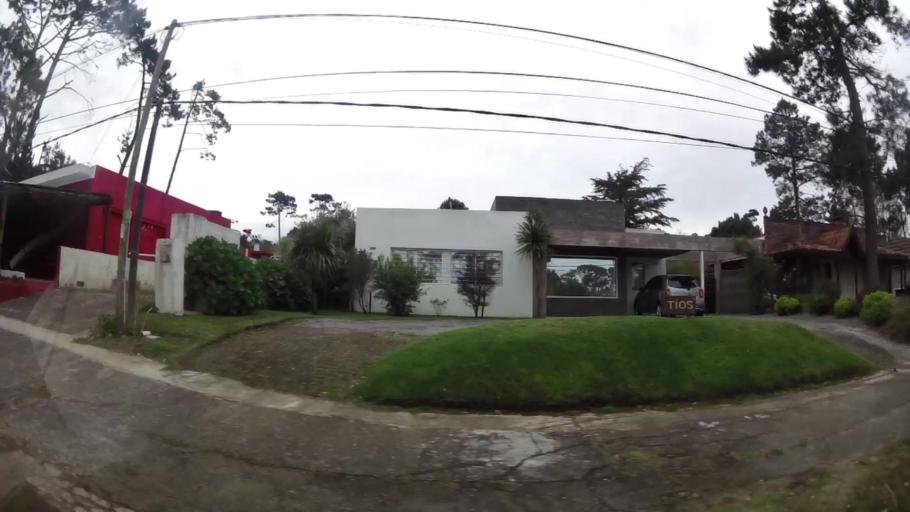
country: UY
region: Maldonado
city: Maldonado
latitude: -34.9094
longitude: -54.9854
